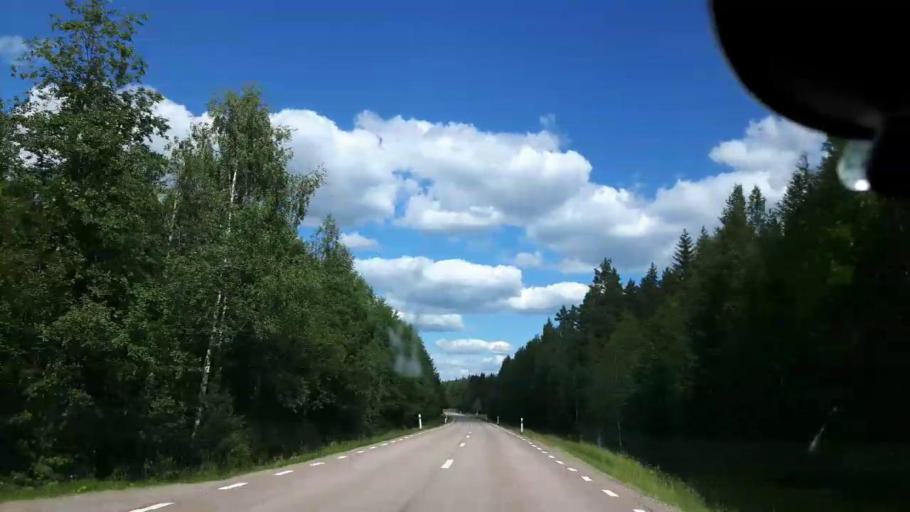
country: SE
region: Jaemtland
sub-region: Ragunda Kommun
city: Hammarstrand
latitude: 62.9039
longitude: 16.7005
